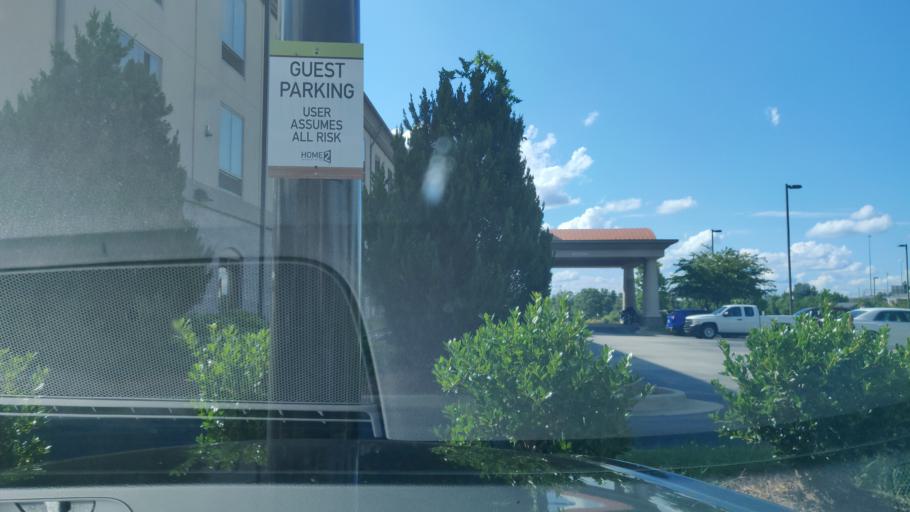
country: US
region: Alabama
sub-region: Lee County
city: Opelika
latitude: 32.6123
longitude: -85.4011
